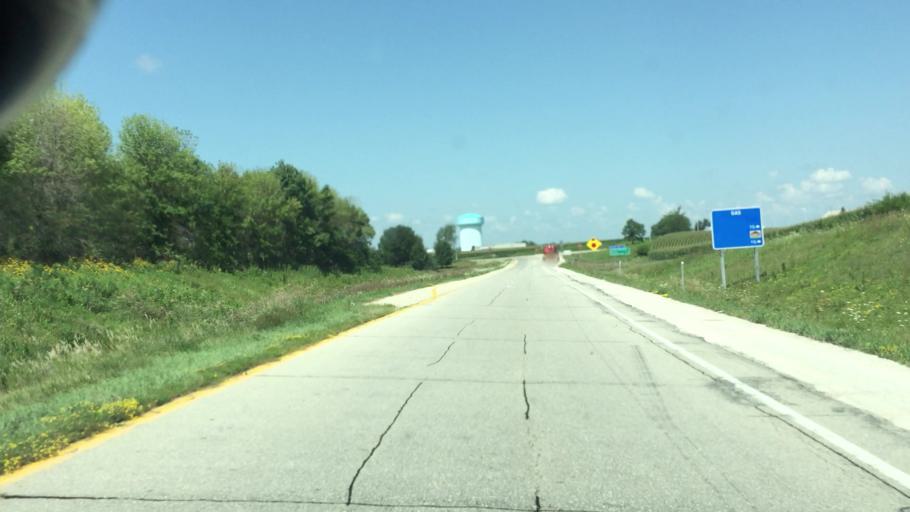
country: US
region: Iowa
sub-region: Jasper County
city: Newton
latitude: 41.6831
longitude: -92.9967
